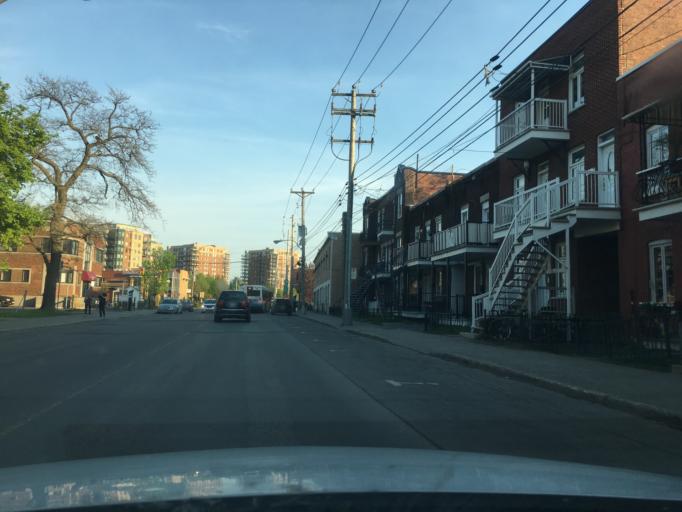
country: CA
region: Quebec
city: Westmount
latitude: 45.4635
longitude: -73.5642
